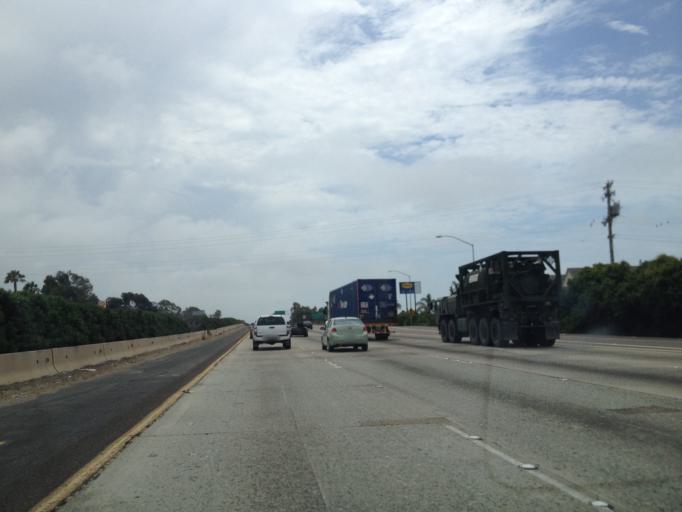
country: US
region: California
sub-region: San Diego County
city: Carlsbad
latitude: 33.1661
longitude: -117.3438
